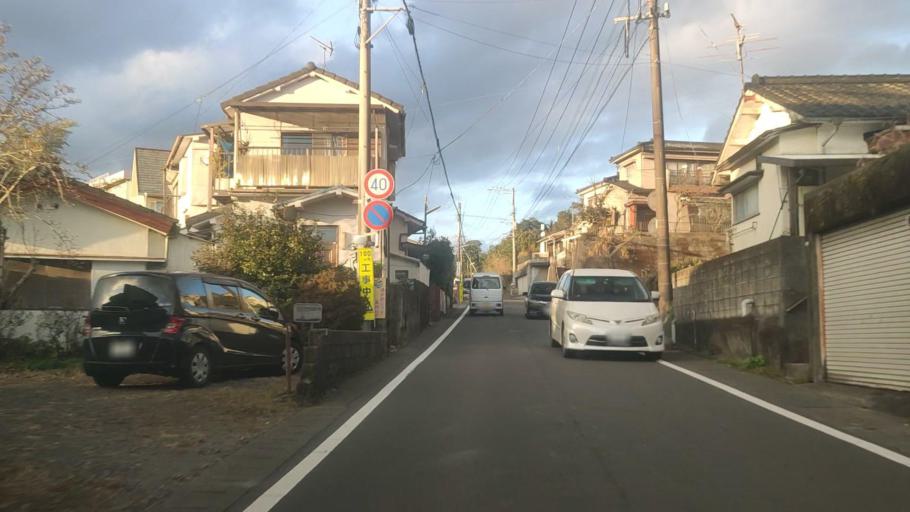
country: JP
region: Kagoshima
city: Kagoshima-shi
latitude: 31.6224
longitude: 130.5529
